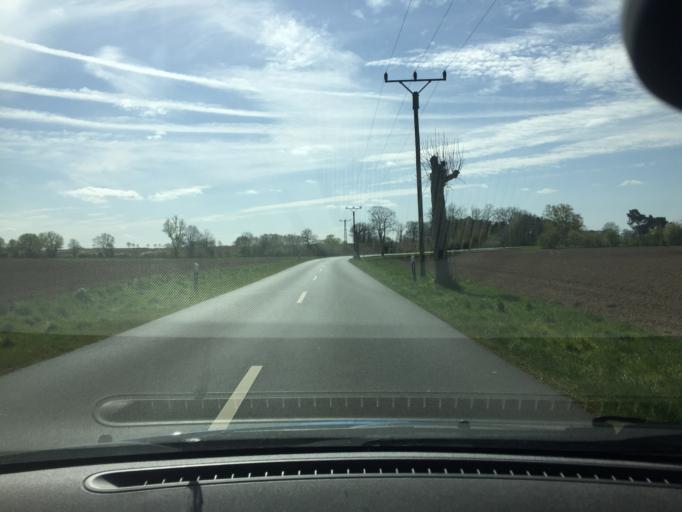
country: DE
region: Lower Saxony
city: Ratzlingen
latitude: 52.9720
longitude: 10.6782
